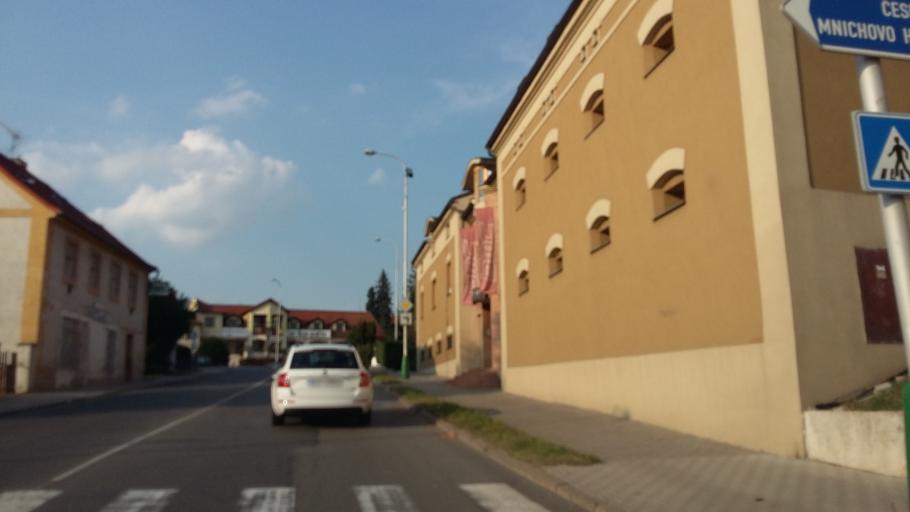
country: CZ
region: Central Bohemia
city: Kosmonosy
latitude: 50.4387
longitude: 14.9298
